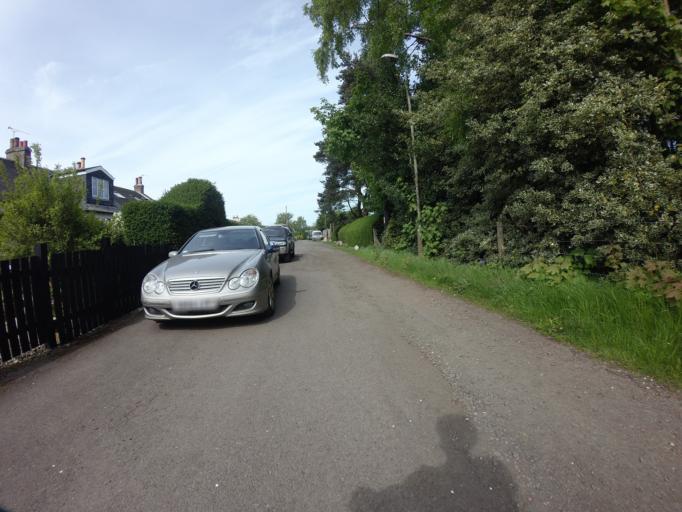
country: GB
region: Scotland
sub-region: West Lothian
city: Broxburn
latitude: 55.9185
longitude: -3.4839
